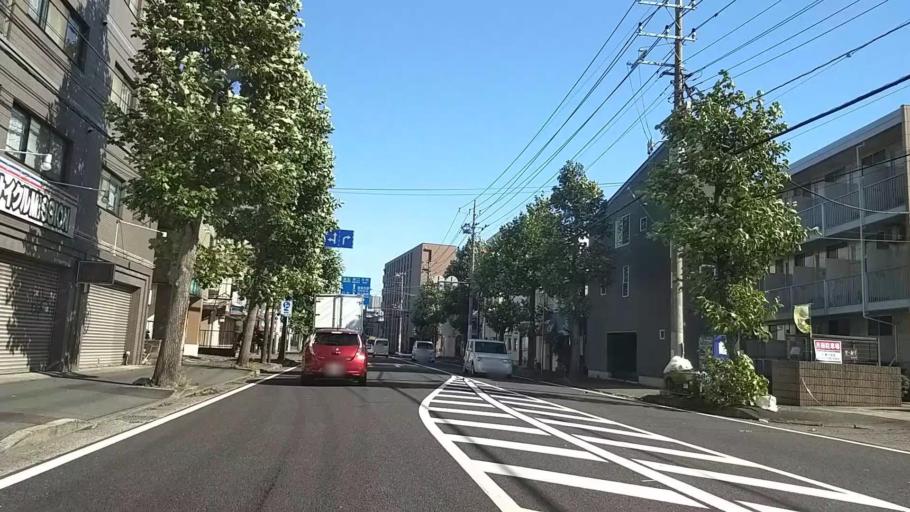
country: JP
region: Kanagawa
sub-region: Kawasaki-shi
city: Kawasaki
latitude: 35.5511
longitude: 139.6592
